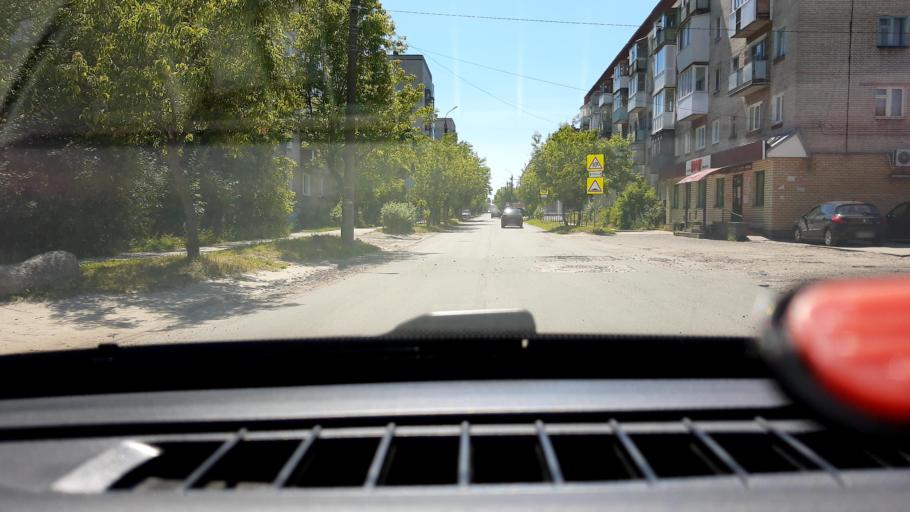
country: RU
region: Nizjnij Novgorod
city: Dzerzhinsk
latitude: 56.2533
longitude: 43.4744
